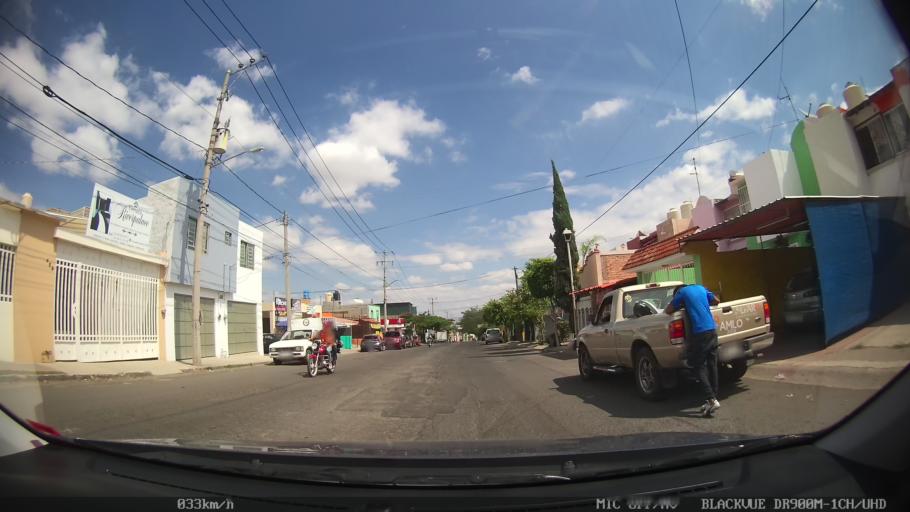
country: MX
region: Jalisco
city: Tonala
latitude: 20.6324
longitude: -103.2502
